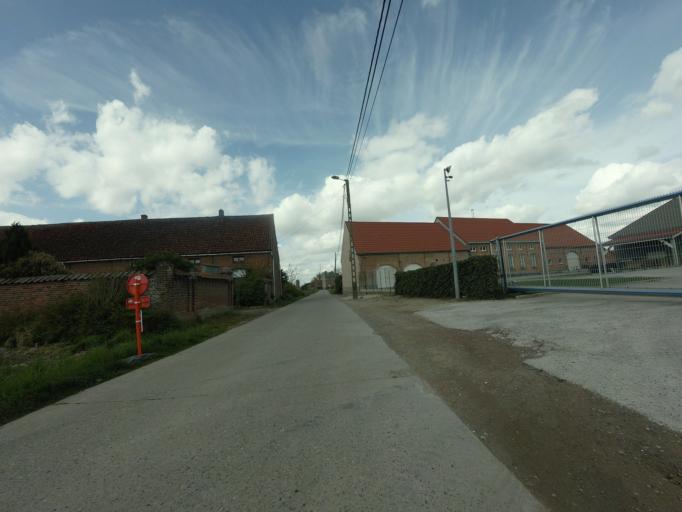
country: BE
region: Flanders
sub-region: Provincie Vlaams-Brabant
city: Kapelle-op-den-Bos
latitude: 51.0230
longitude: 4.4133
